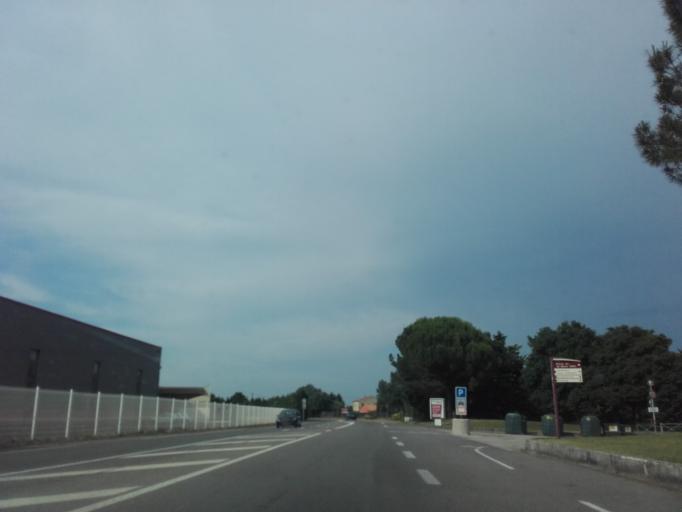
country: FR
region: Rhone-Alpes
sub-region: Departement de la Drome
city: Loriol-sur-Drome
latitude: 44.7544
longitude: 4.8190
